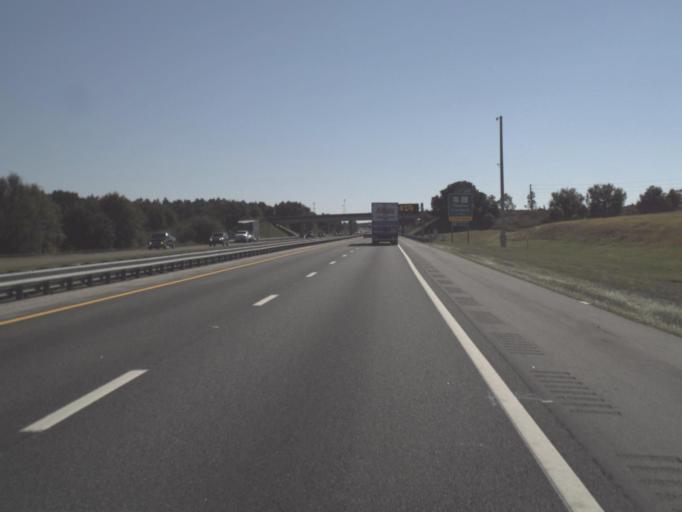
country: US
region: Florida
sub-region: Lake County
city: Hawthorne
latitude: 28.6866
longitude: -81.8664
